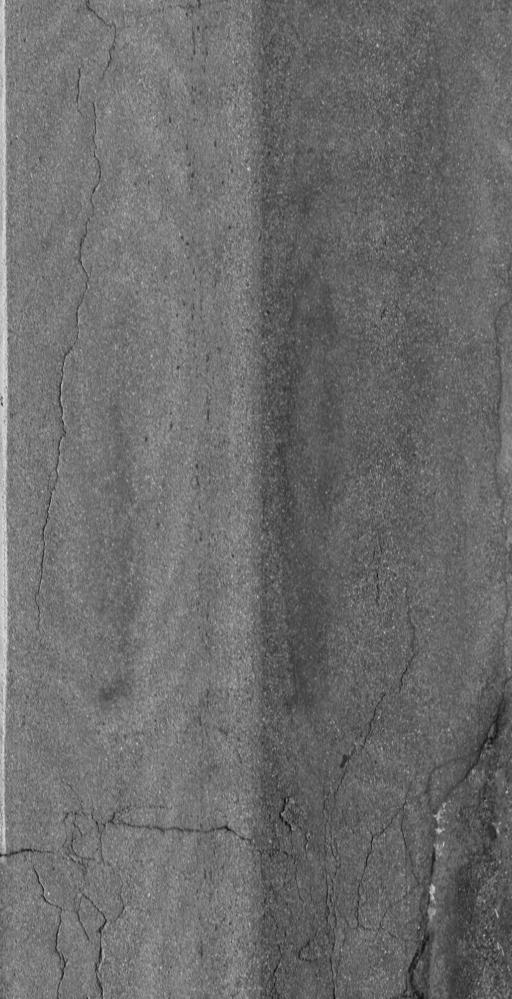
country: US
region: Vermont
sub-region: Chittenden County
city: Essex Junction
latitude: 44.5050
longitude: -73.1278
